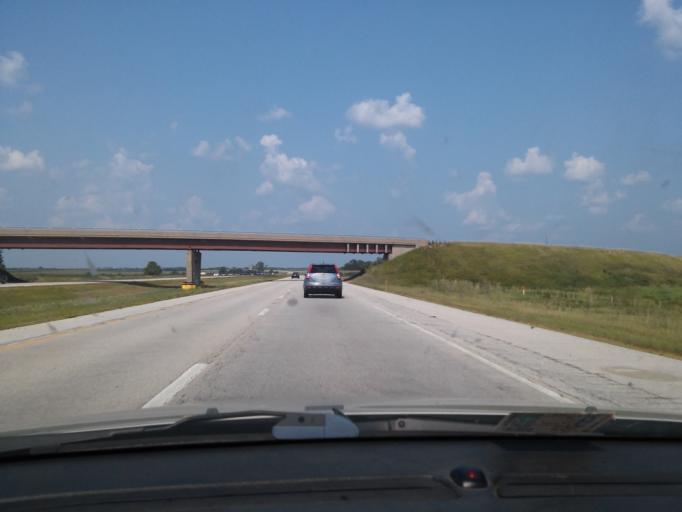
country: US
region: Illinois
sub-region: Livingston County
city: Pontiac
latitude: 40.9415
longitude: -88.5930
